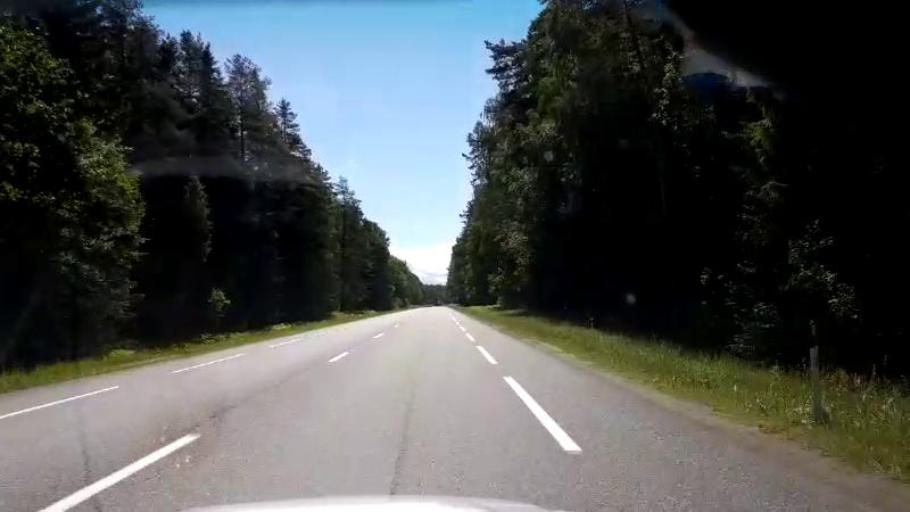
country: LV
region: Saulkrastu
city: Saulkrasti
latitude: 57.3735
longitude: 24.4344
